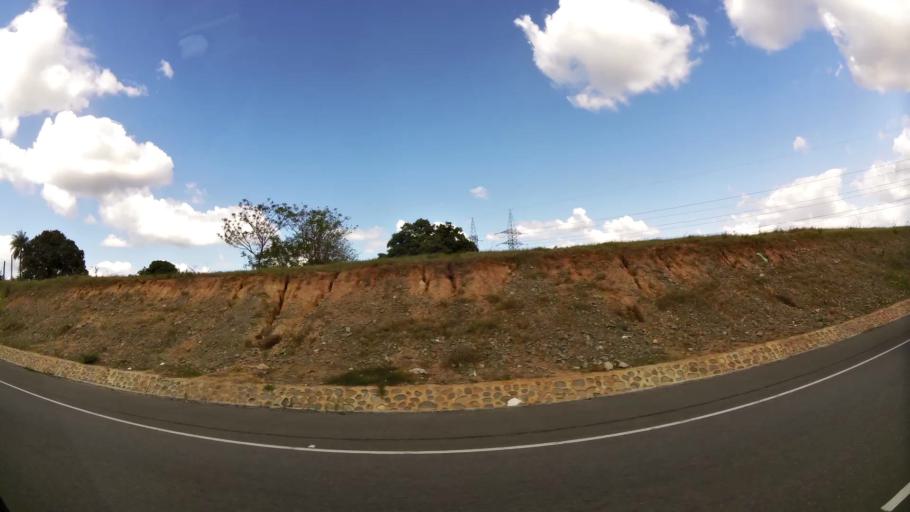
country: DO
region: Santo Domingo
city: Santo Domingo Oeste
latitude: 18.5398
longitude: -70.0778
